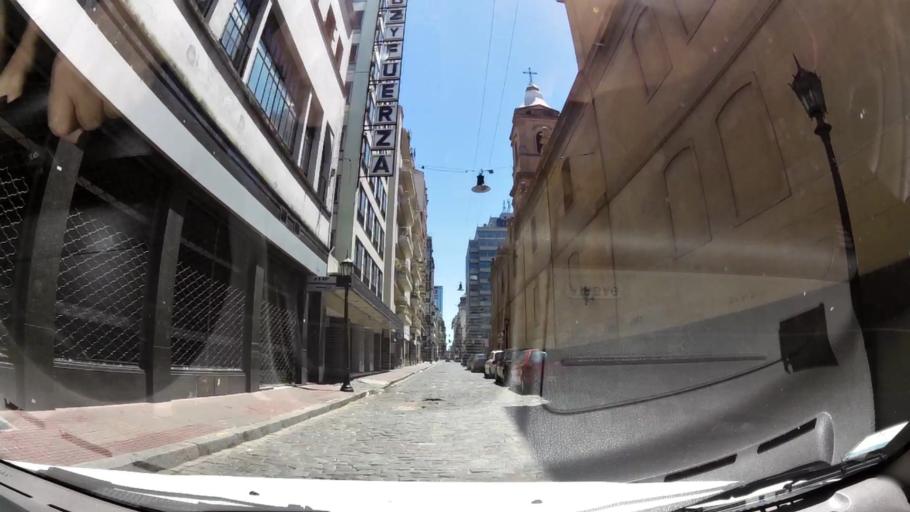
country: AR
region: Buenos Aires F.D.
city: Buenos Aires
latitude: -34.6133
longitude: -58.3719
